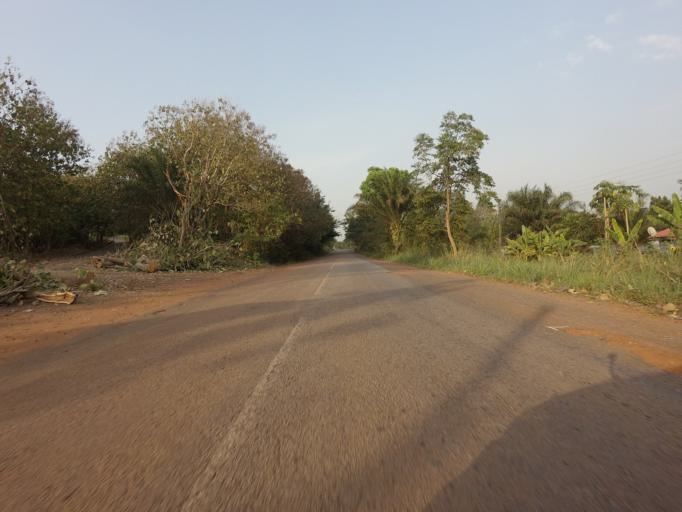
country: GH
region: Volta
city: Ho
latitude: 6.5498
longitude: 0.2928
